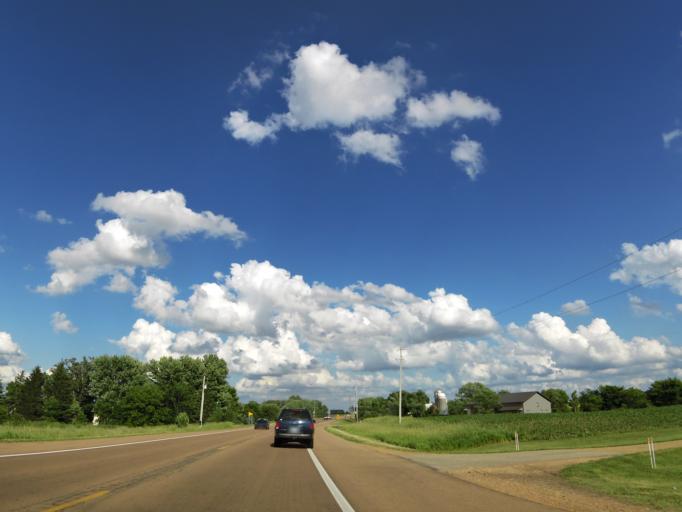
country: US
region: Minnesota
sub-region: Carver County
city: Victoria
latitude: 44.8115
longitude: -93.6693
